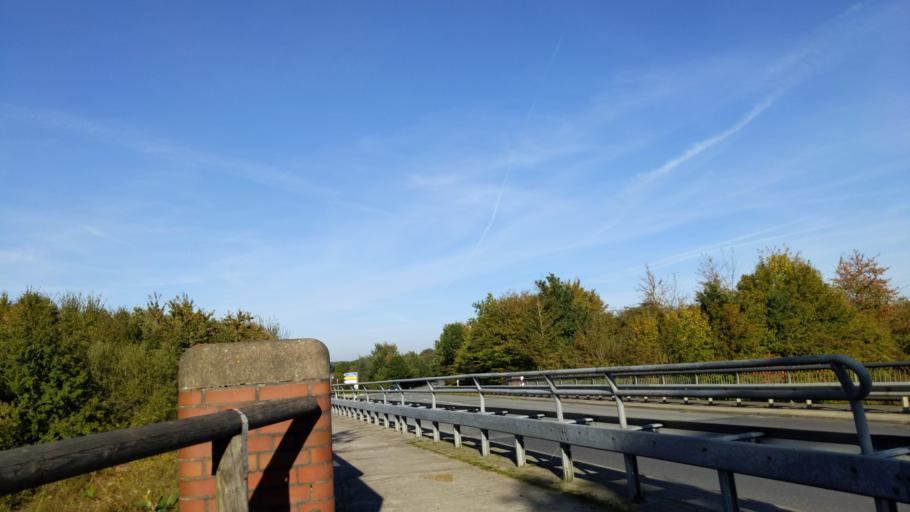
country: DE
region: Schleswig-Holstein
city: Eutin
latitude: 54.1226
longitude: 10.5991
